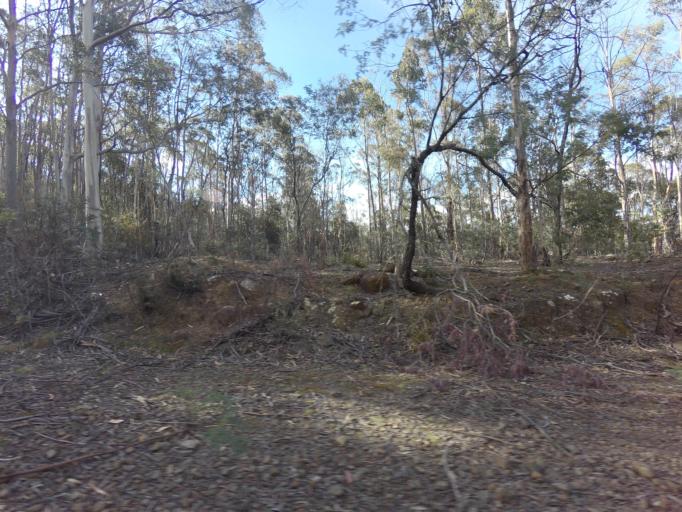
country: AU
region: Tasmania
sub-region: Break O'Day
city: St Helens
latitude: -41.8378
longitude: 148.0706
